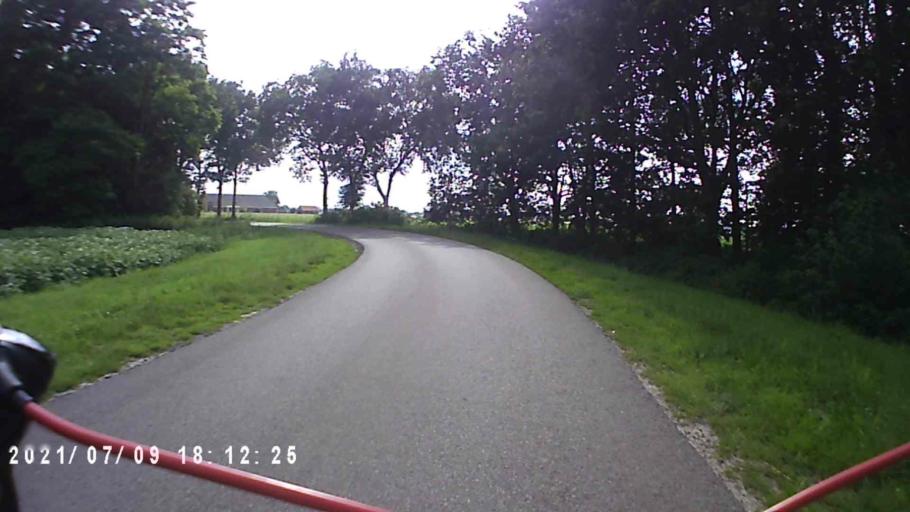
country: NL
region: Groningen
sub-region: Gemeente Pekela
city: Oude Pekela
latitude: 53.0666
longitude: 7.0294
